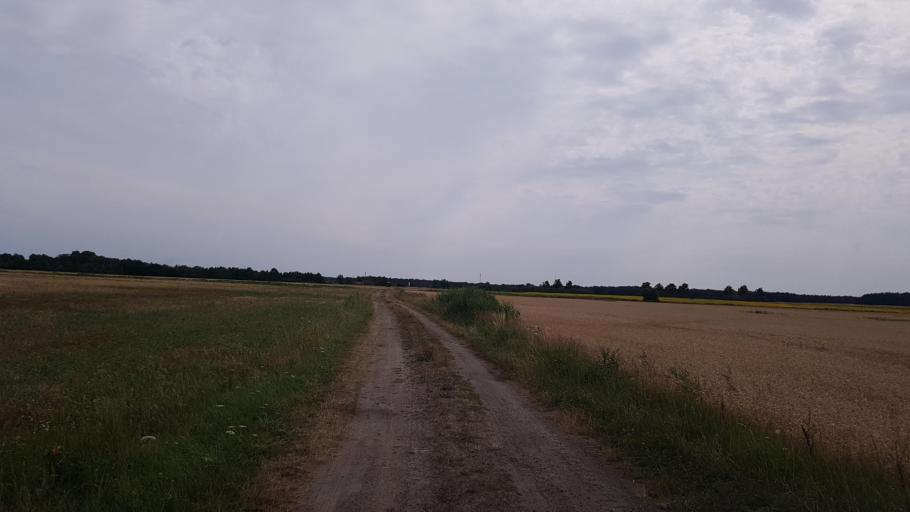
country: DE
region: Brandenburg
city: Bronkow
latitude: 51.5955
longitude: 13.9339
